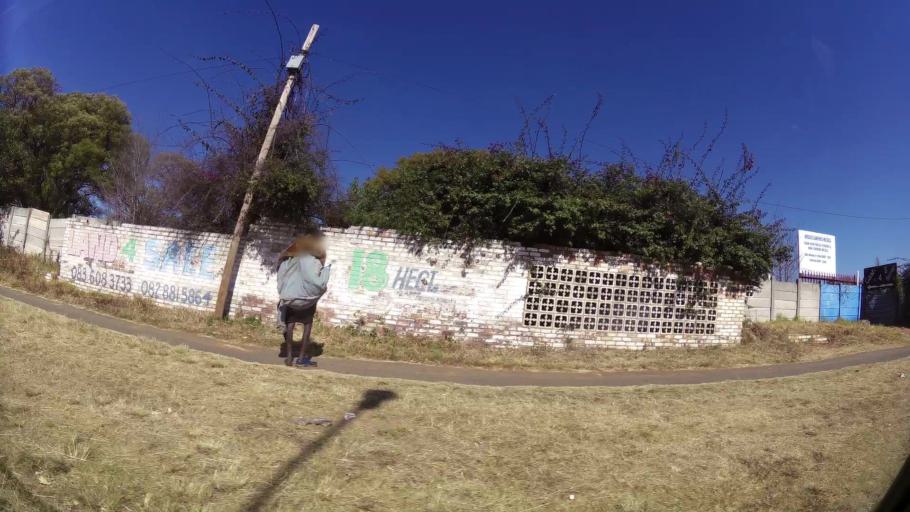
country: ZA
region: Gauteng
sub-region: City of Johannesburg Metropolitan Municipality
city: Johannesburg
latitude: -26.2404
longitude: 28.0783
